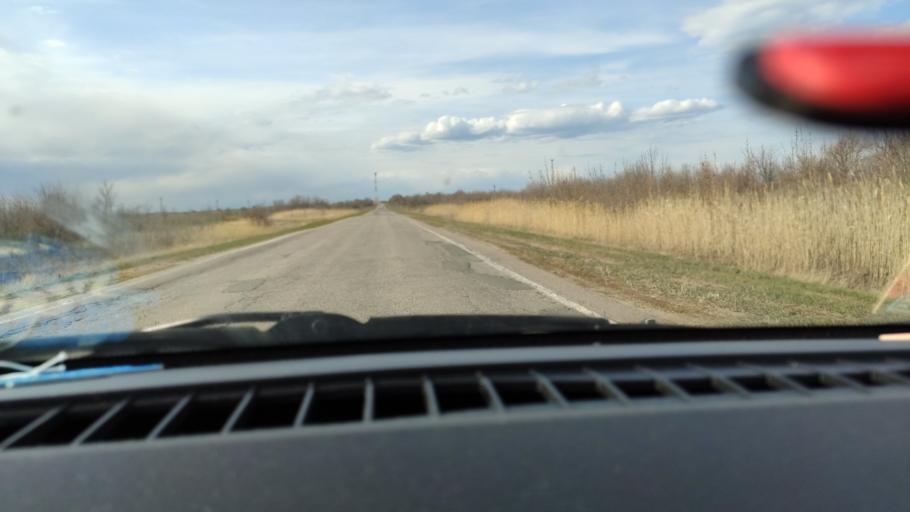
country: RU
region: Saratov
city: Rovnoye
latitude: 51.0138
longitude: 46.0967
